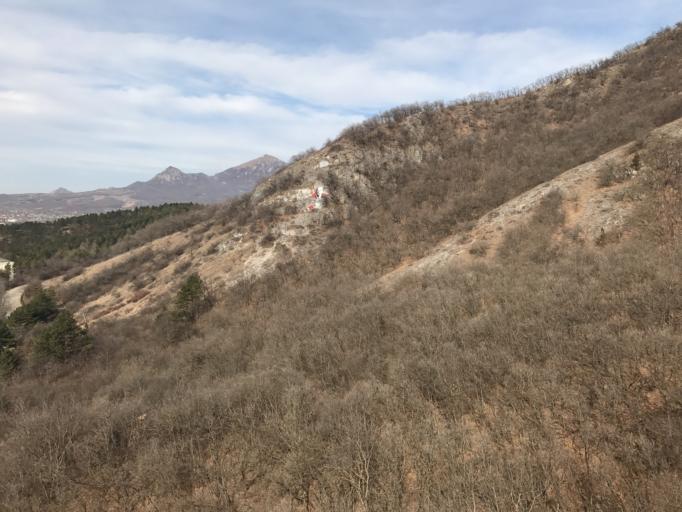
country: RU
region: Stavropol'skiy
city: Goryachevodskiy
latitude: 44.0454
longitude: 43.0834
